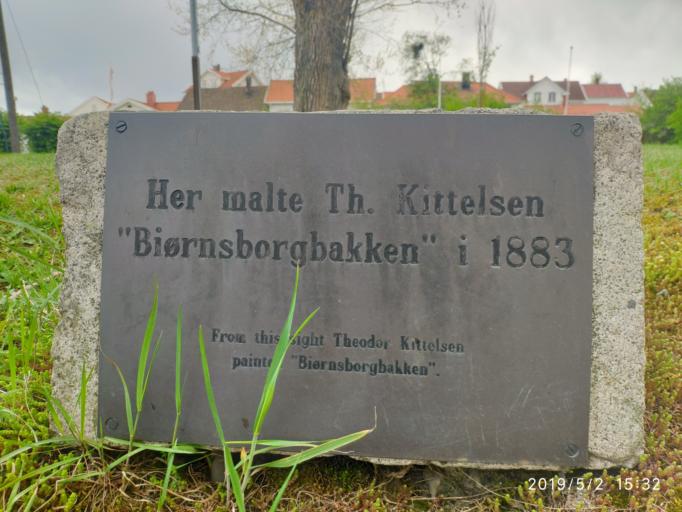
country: NO
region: Telemark
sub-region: Kragero
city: Kragero
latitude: 58.8711
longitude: 9.4128
